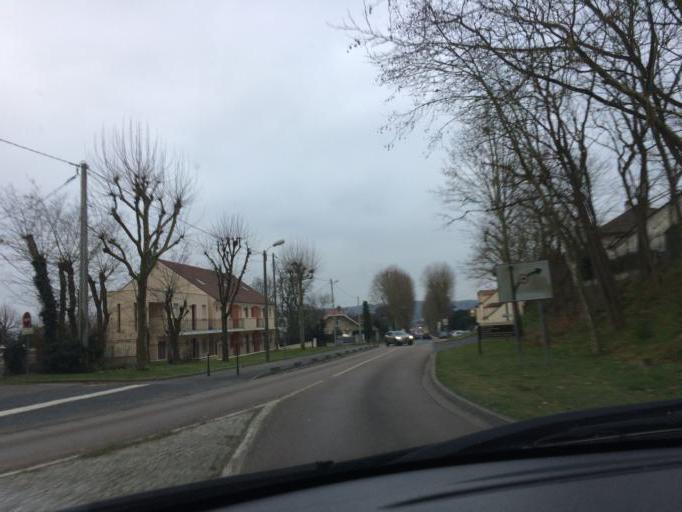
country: FR
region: Ile-de-France
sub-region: Departement de l'Essonne
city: Etrechy
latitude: 48.4979
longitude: 2.1955
